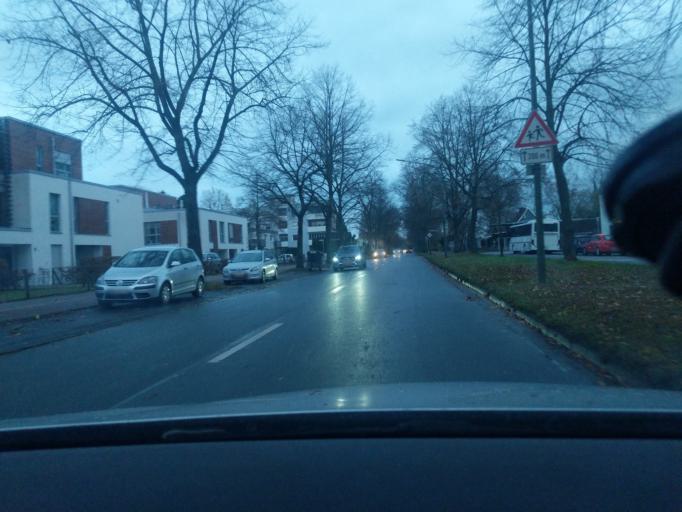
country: DE
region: North Rhine-Westphalia
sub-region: Regierungsbezirk Arnsberg
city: Hamm
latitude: 51.6924
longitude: 7.8593
